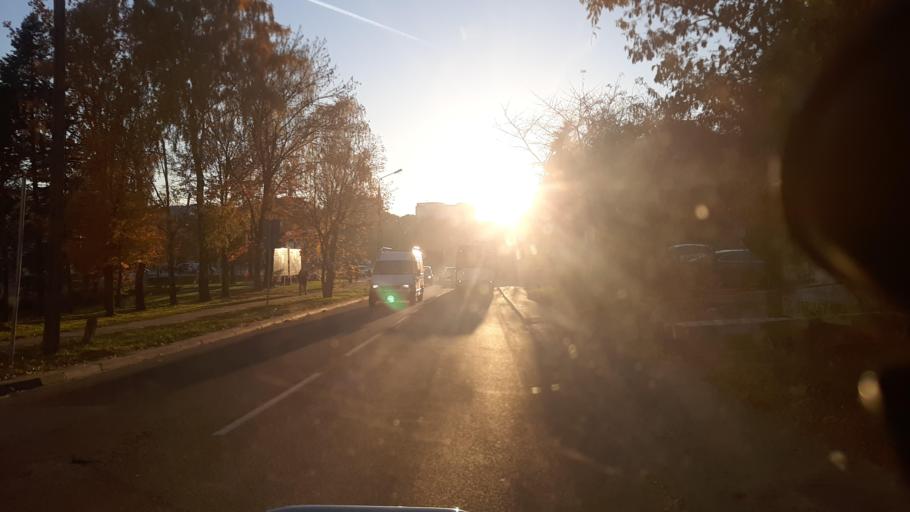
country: PL
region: Lublin Voivodeship
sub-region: Powiat lubelski
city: Lublin
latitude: 51.2543
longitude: 22.5625
